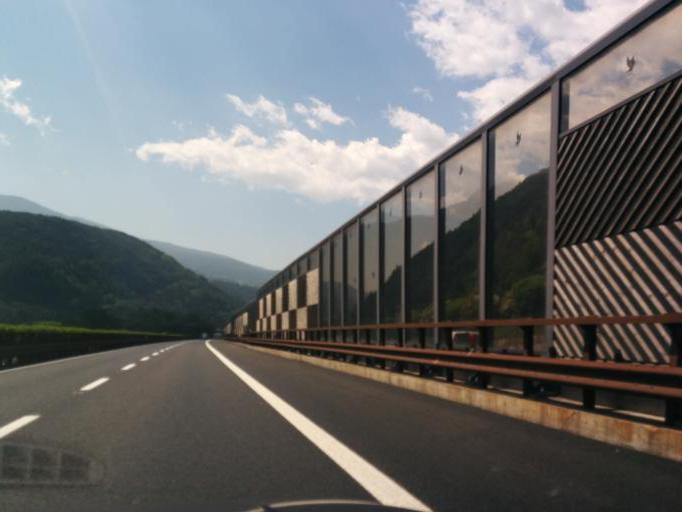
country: IT
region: Trentino-Alto Adige
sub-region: Bolzano
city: Velturno
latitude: 46.6786
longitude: 11.6217
